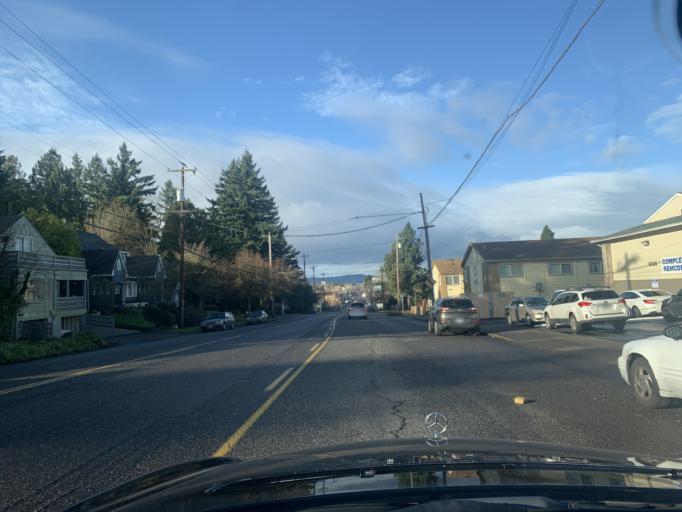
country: US
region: Oregon
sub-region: Multnomah County
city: Lents
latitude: 45.5265
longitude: -122.5975
